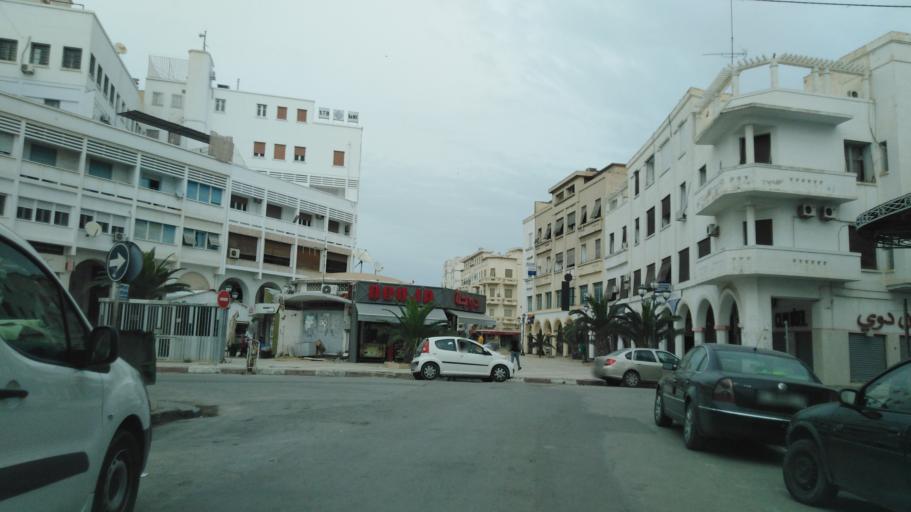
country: TN
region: Safaqis
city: Sfax
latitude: 34.7329
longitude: 10.7622
